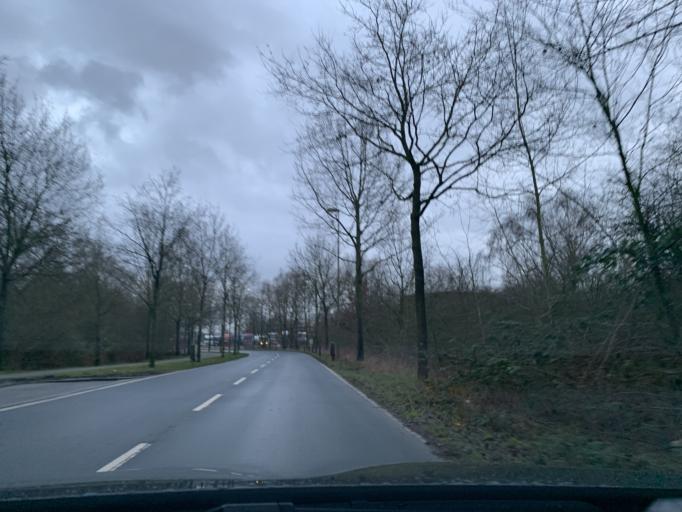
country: DE
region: Lower Saxony
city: Ritterhude
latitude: 53.1414
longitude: 8.7100
